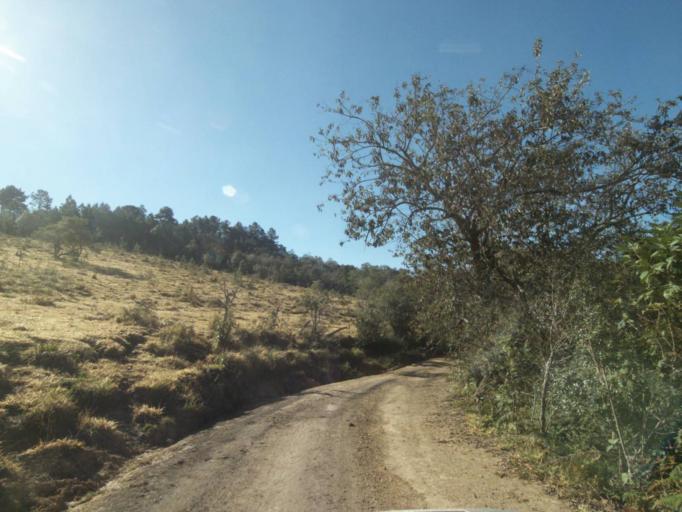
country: BR
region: Parana
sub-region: Tibagi
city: Tibagi
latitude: -24.5797
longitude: -50.4811
